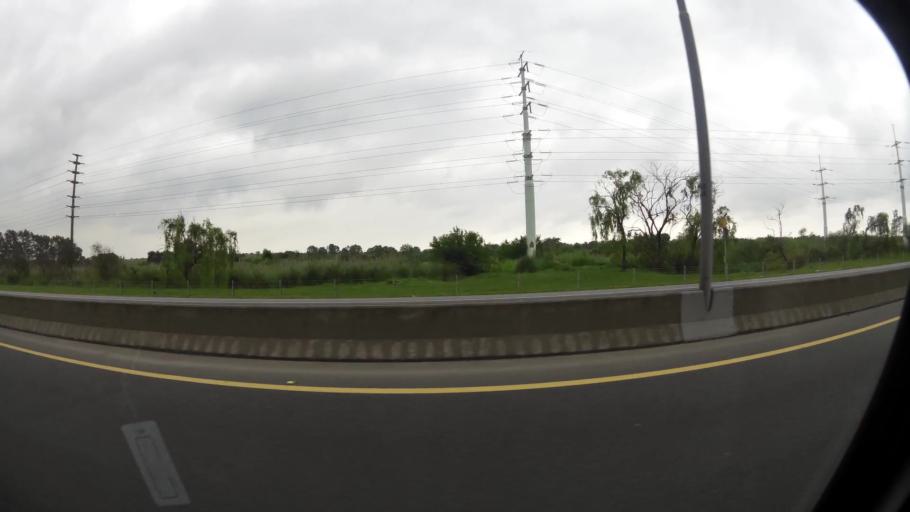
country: AR
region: Buenos Aires
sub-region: Partido de Quilmes
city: Quilmes
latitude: -34.6879
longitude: -58.2946
